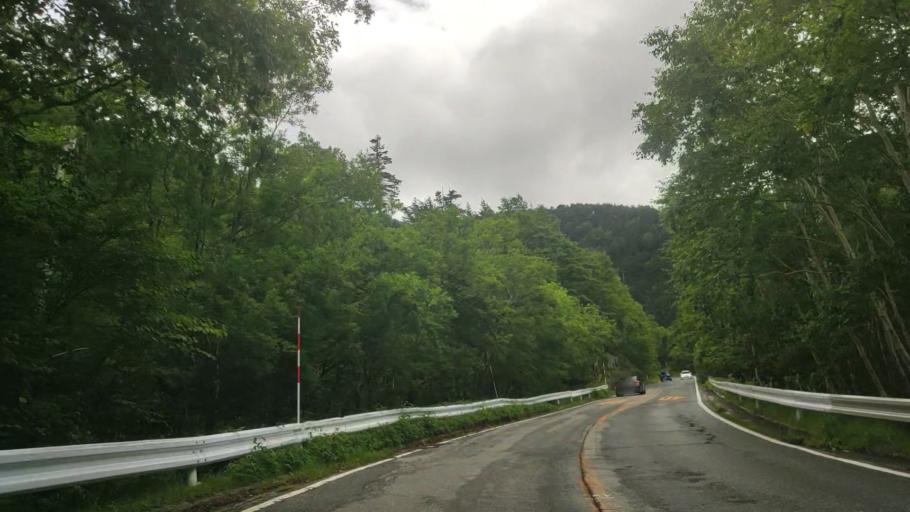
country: JP
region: Tochigi
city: Nikko
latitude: 36.8253
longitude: 139.3927
